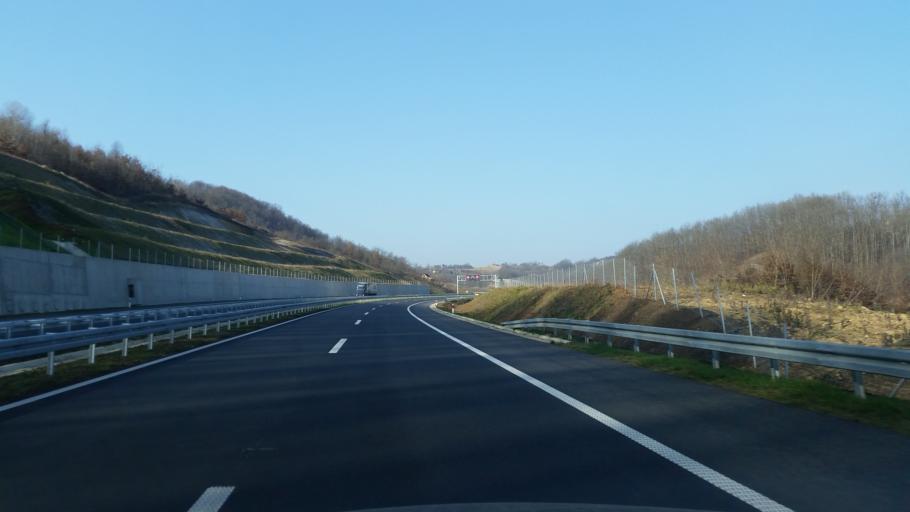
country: RS
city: Prislonica
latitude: 44.0074
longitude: 20.3887
